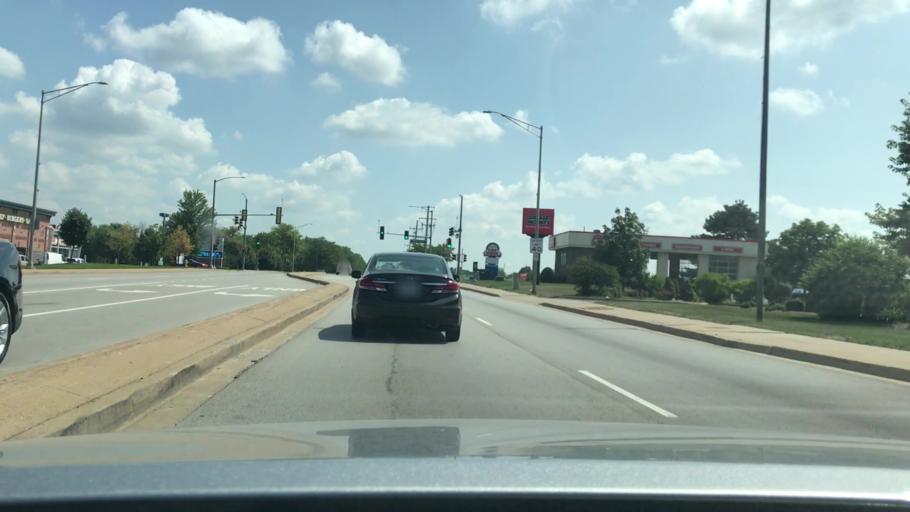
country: US
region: Illinois
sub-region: Will County
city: Bolingbrook
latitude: 41.7112
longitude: -88.0678
